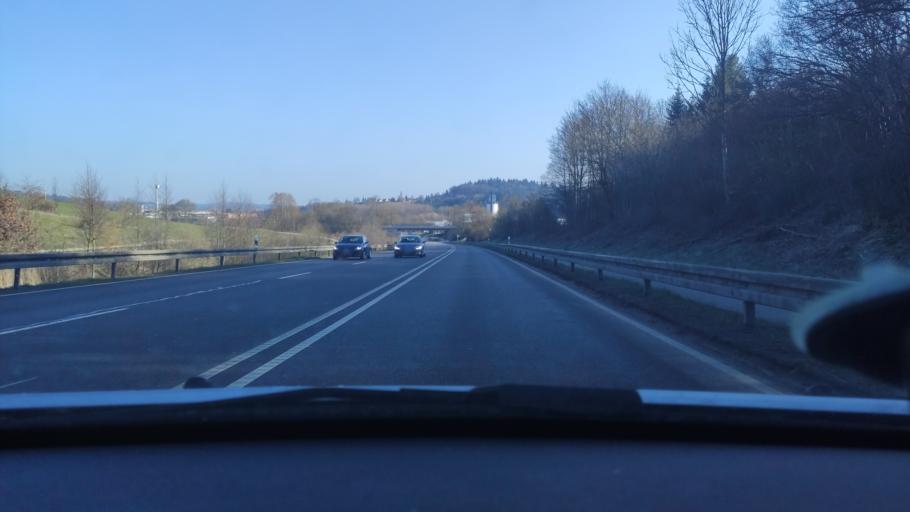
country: DE
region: Baden-Wuerttemberg
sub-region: Tuebingen Region
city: Balingen
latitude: 48.2494
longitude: 8.8539
